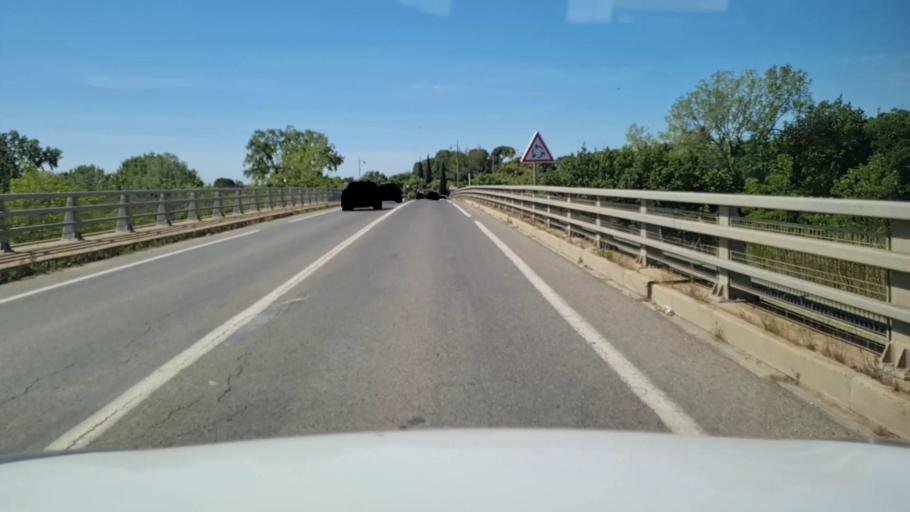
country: FR
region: Languedoc-Roussillon
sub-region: Departement du Gard
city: Sommieres
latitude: 43.7905
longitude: 4.0831
